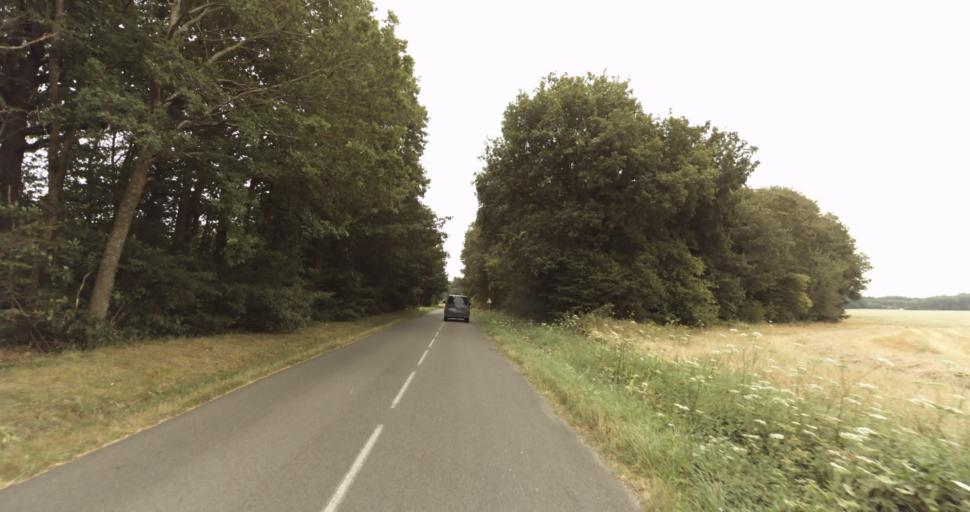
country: FR
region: Haute-Normandie
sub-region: Departement de l'Eure
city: Marcilly-sur-Eure
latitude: 48.8199
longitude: 1.3082
